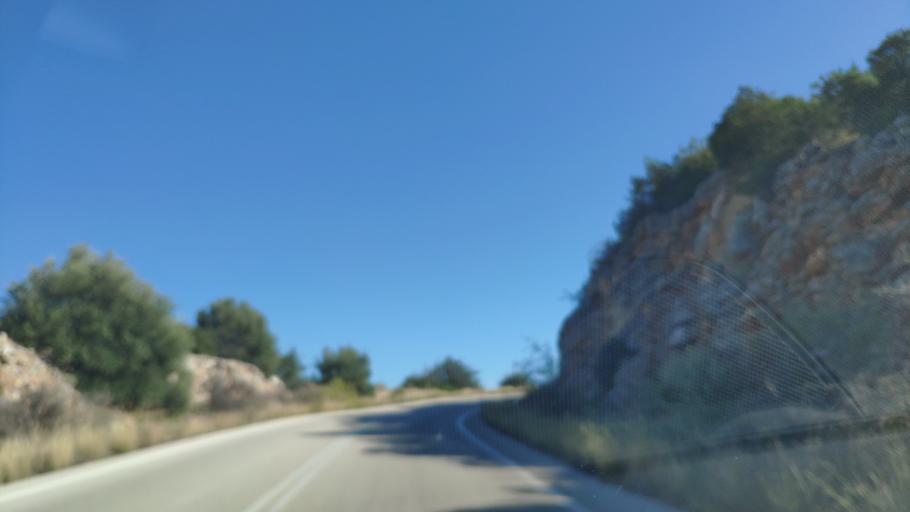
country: GR
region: Peloponnese
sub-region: Nomos Argolidos
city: Palaia Epidavros
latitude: 37.6284
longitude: 23.1422
